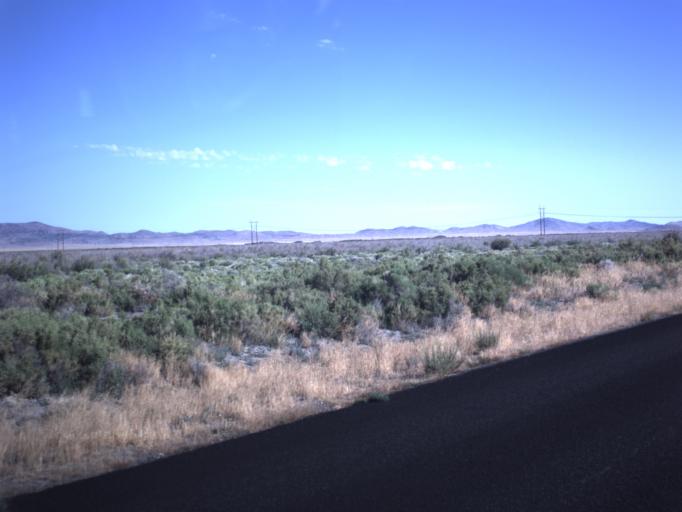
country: US
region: Utah
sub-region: Beaver County
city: Milford
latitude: 38.5648
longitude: -112.9905
